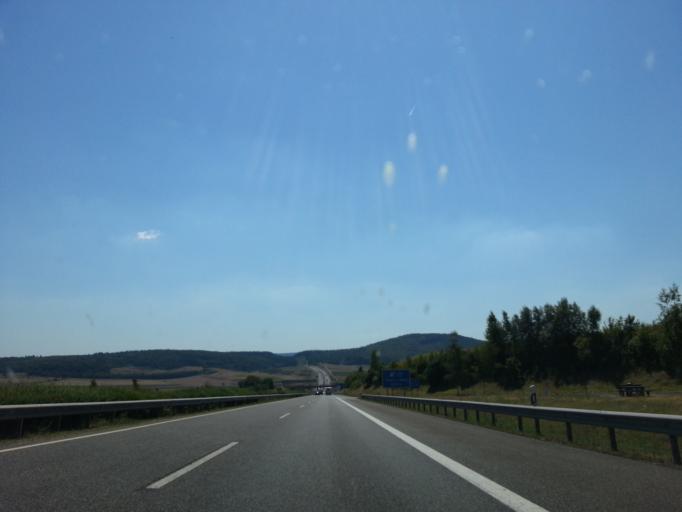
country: DE
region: Rheinland-Pfalz
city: Bergweiler
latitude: 49.9688
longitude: 6.8362
